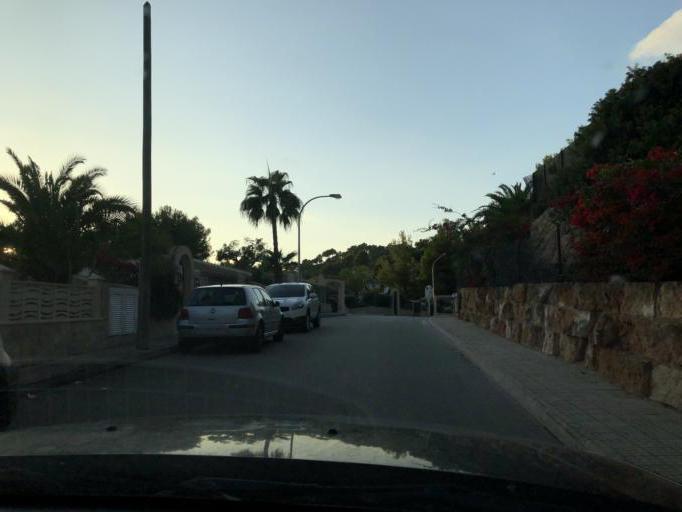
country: ES
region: Balearic Islands
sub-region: Illes Balears
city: Santa Ponsa
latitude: 39.5270
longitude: 2.4806
